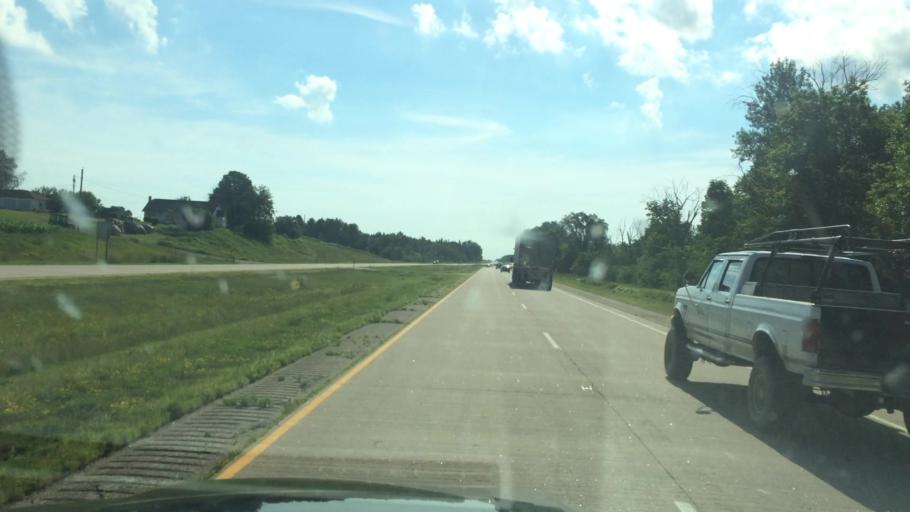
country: US
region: Wisconsin
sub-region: Waupaca County
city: Marion
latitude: 44.8041
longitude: -88.9665
